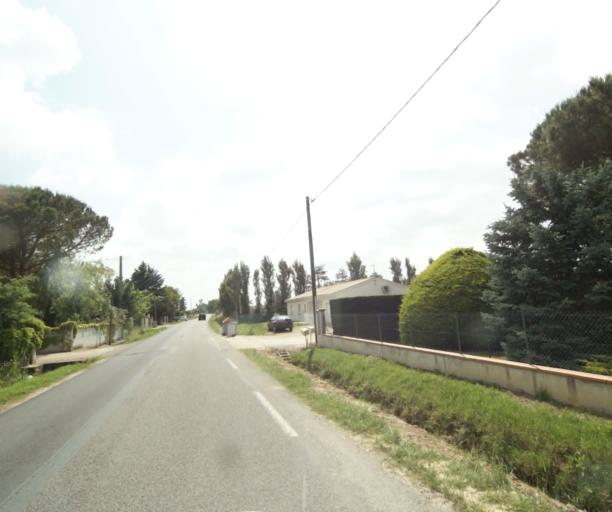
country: FR
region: Midi-Pyrenees
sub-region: Departement du Tarn-et-Garonne
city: Montauban
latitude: 44.0463
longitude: 1.3814
